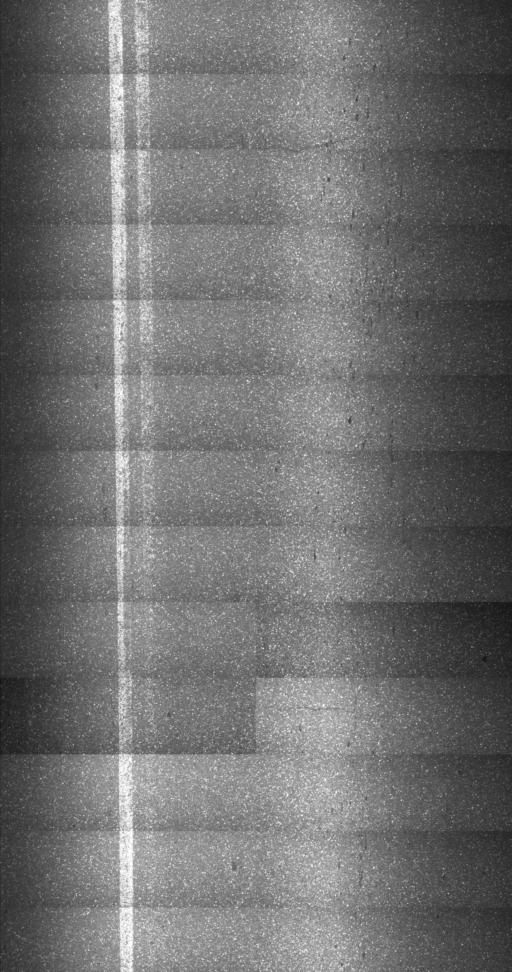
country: US
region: Vermont
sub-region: Caledonia County
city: Hardwick
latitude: 44.4996
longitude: -72.3717
